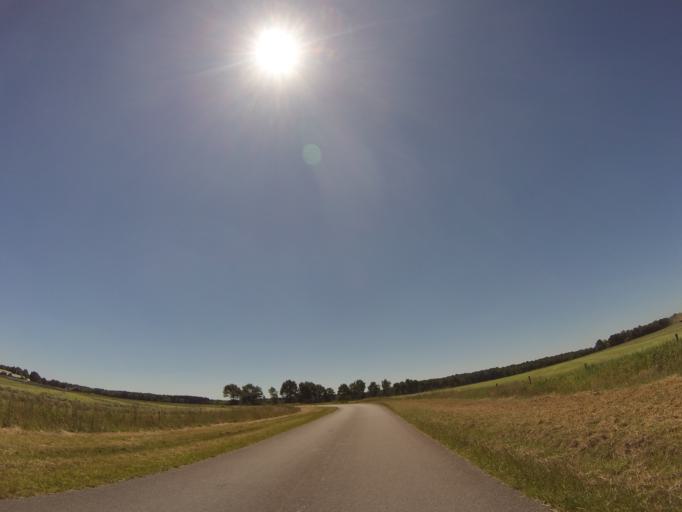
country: NL
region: Drenthe
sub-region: Gemeente Assen
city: Assen
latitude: 52.9403
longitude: 6.5754
